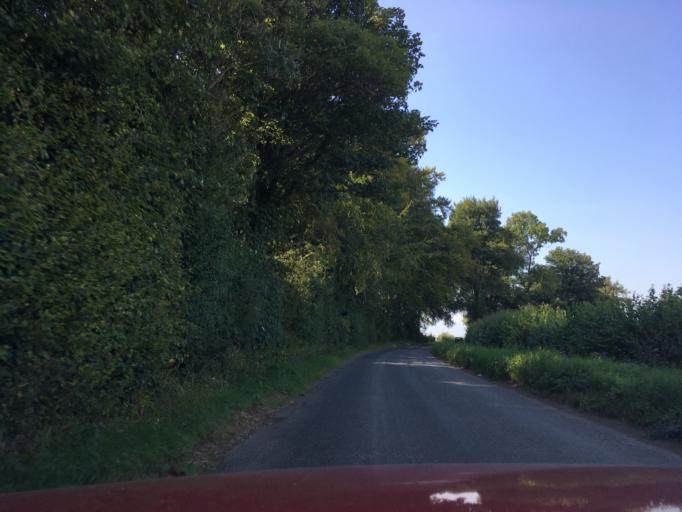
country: GB
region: England
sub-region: Gloucestershire
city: Dursley
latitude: 51.6706
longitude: -2.2916
